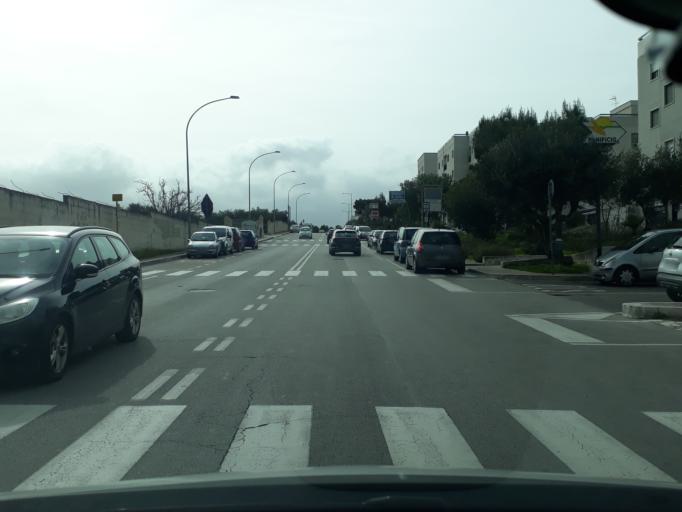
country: IT
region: Apulia
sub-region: Provincia di Bari
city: Monopoli
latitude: 40.9454
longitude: 17.2934
